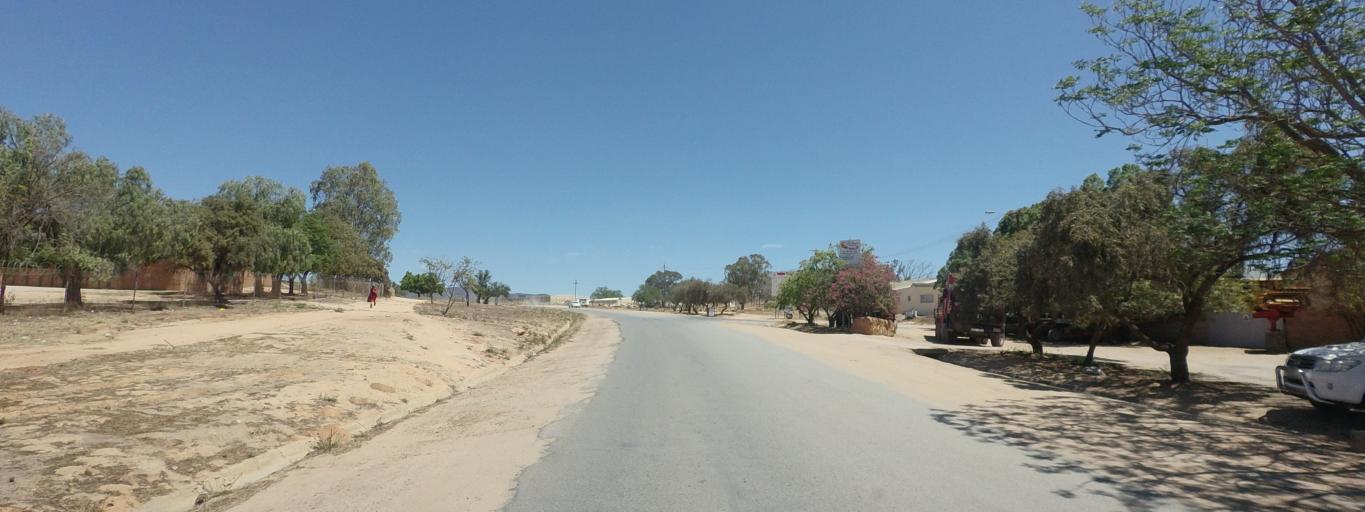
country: ZA
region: Western Cape
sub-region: West Coast District Municipality
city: Clanwilliam
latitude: -32.1889
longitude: 18.8891
